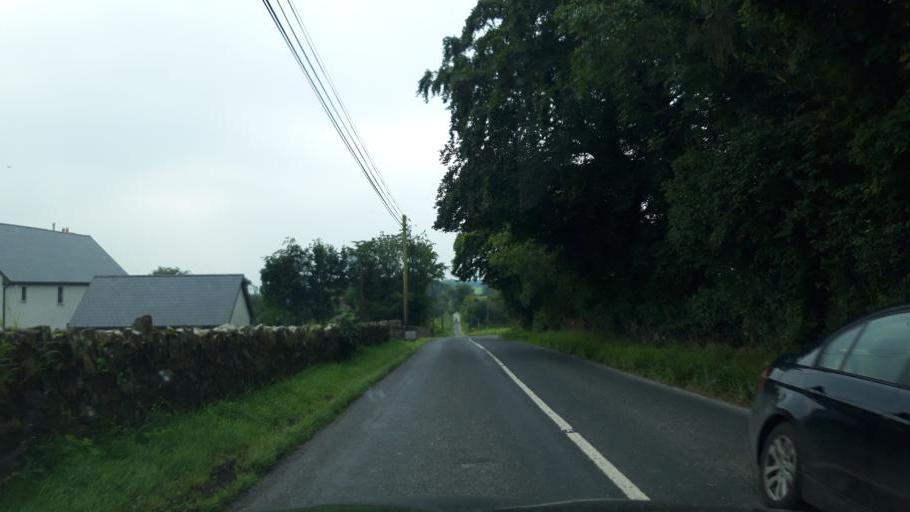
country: IE
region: Munster
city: Fethard
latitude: 52.5519
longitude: -7.6718
